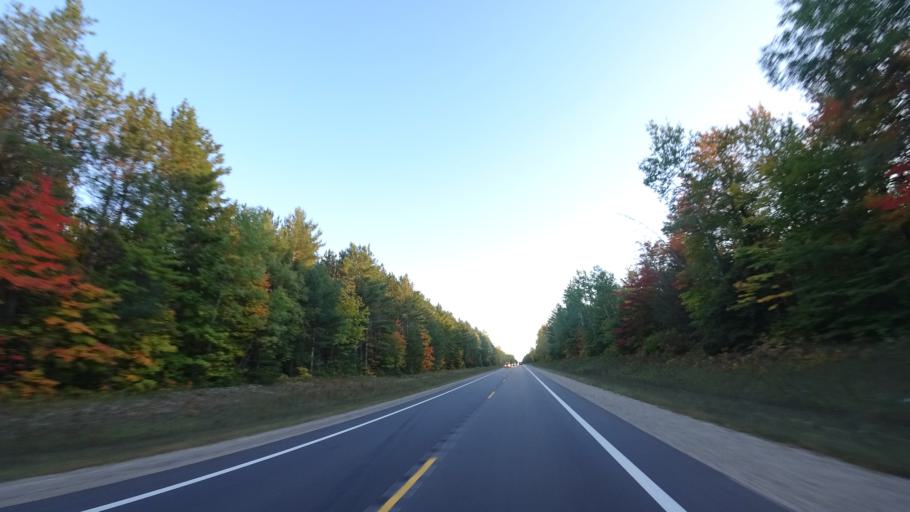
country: US
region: Michigan
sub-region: Luce County
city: Newberry
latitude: 46.3129
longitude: -85.0094
